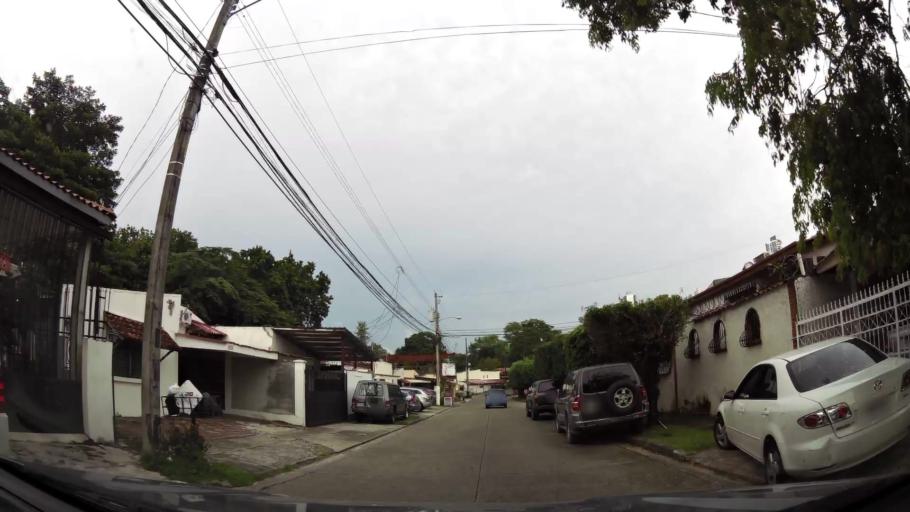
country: PA
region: Panama
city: Panama
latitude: 9.0137
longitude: -79.5394
